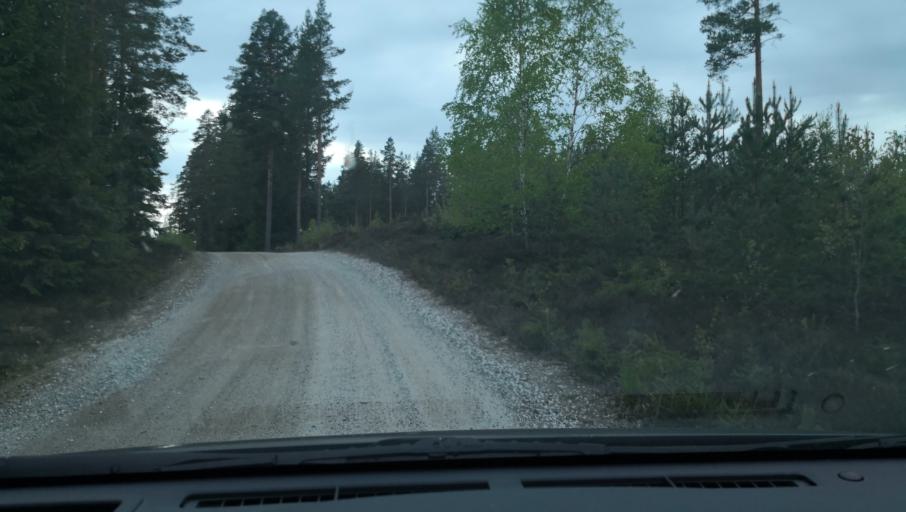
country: SE
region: Vaestmanland
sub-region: Skinnskattebergs Kommun
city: Skinnskatteberg
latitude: 59.8069
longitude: 15.5168
